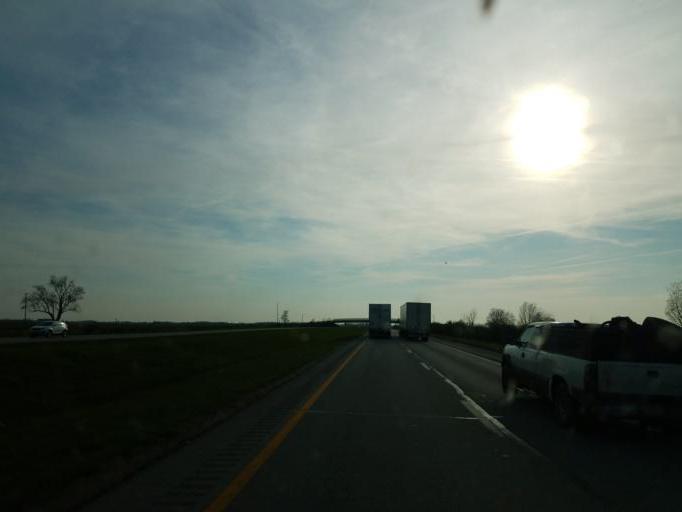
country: US
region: Ohio
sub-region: Greene County
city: Jamestown
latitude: 39.5498
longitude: -83.7407
